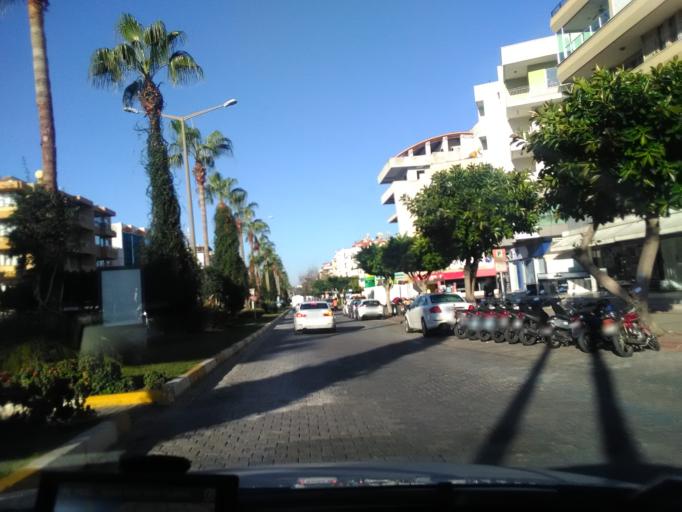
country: TR
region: Antalya
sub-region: Alanya
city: Alanya
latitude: 36.5451
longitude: 31.9935
